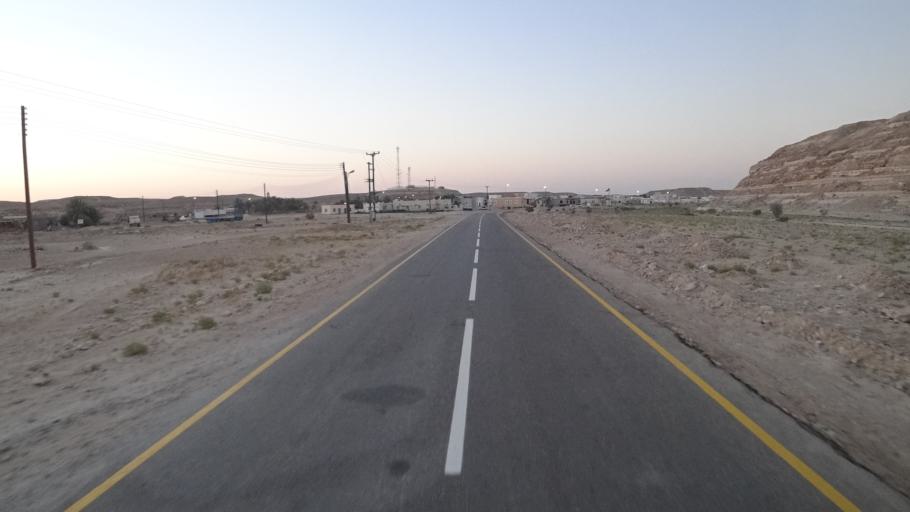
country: OM
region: Zufar
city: Salalah
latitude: 17.4814
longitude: 53.3503
